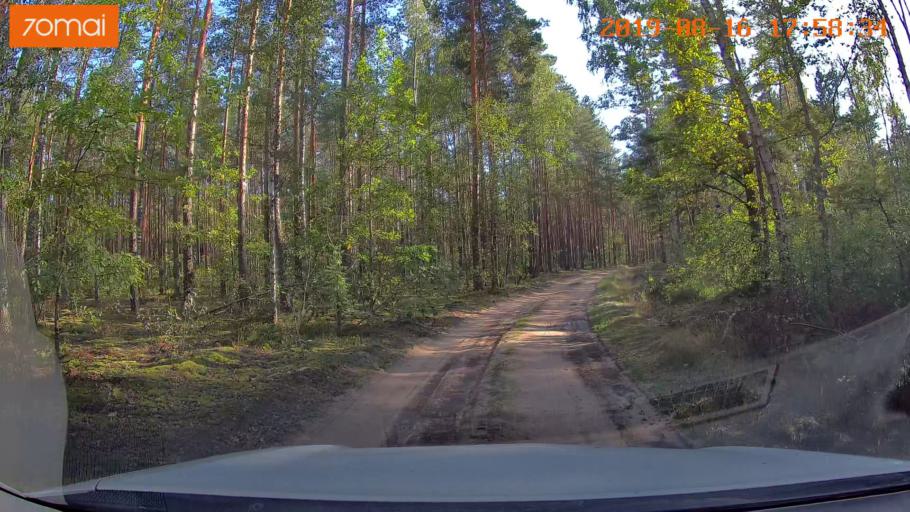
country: BY
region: Mogilev
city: Asipovichy
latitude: 53.2233
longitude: 28.6587
